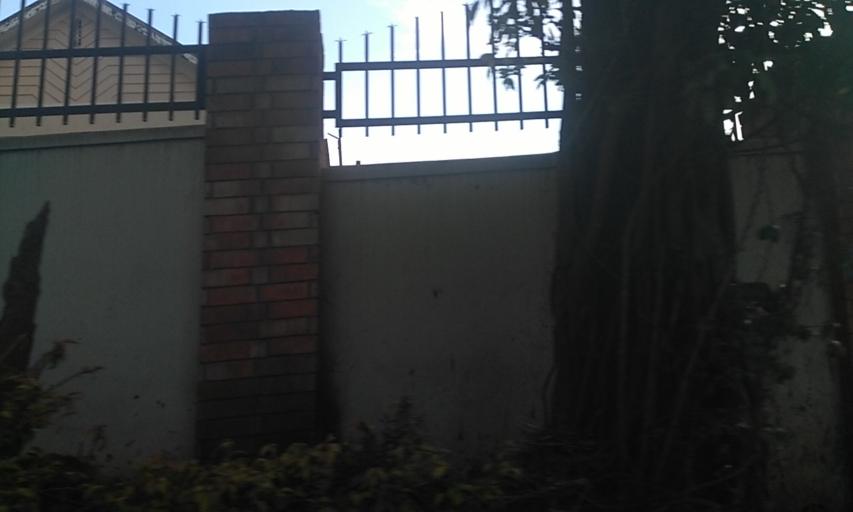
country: UG
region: Central Region
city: Kampala Central Division
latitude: 0.3184
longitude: 32.5558
